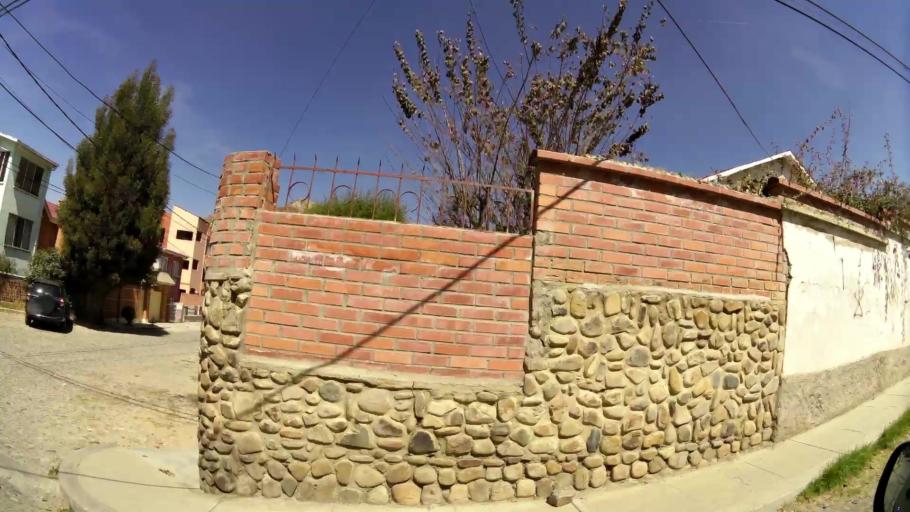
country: BO
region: La Paz
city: La Paz
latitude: -16.5375
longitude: -68.1006
